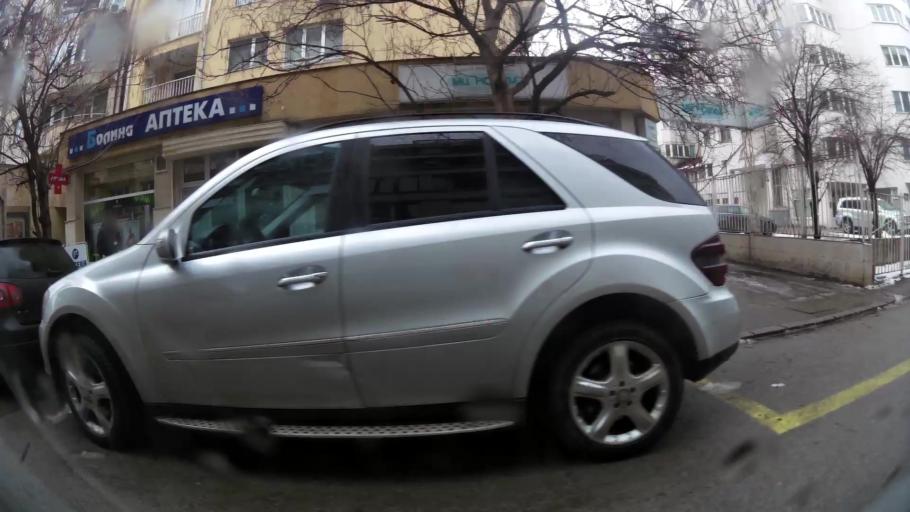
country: BG
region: Sofia-Capital
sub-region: Stolichna Obshtina
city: Sofia
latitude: 42.6720
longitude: 23.2888
